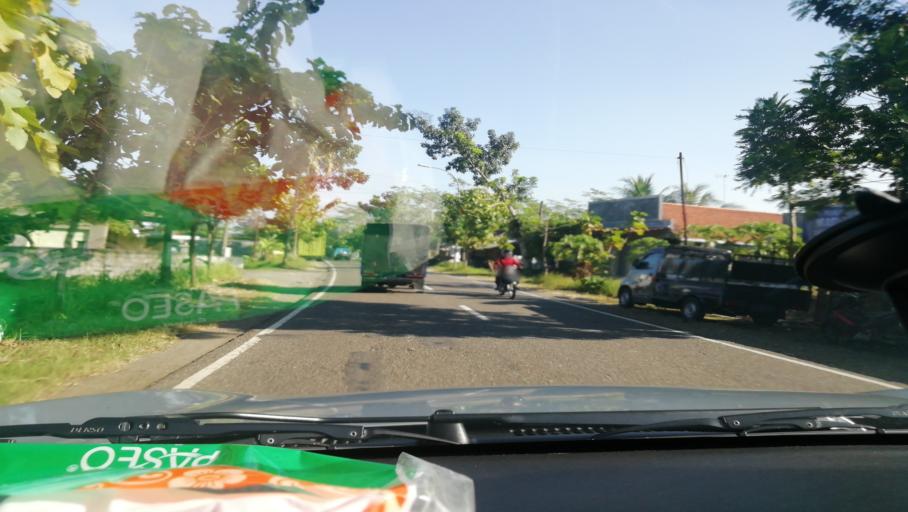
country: ID
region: Central Java
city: Kutoarjo
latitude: -7.6934
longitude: 109.9964
